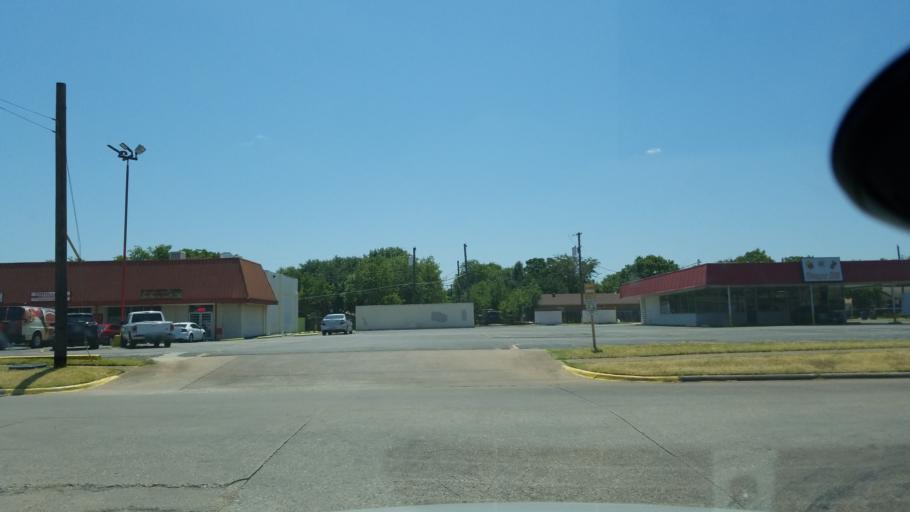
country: US
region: Texas
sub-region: Dallas County
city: Cockrell Hill
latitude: 32.7352
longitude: -96.8843
